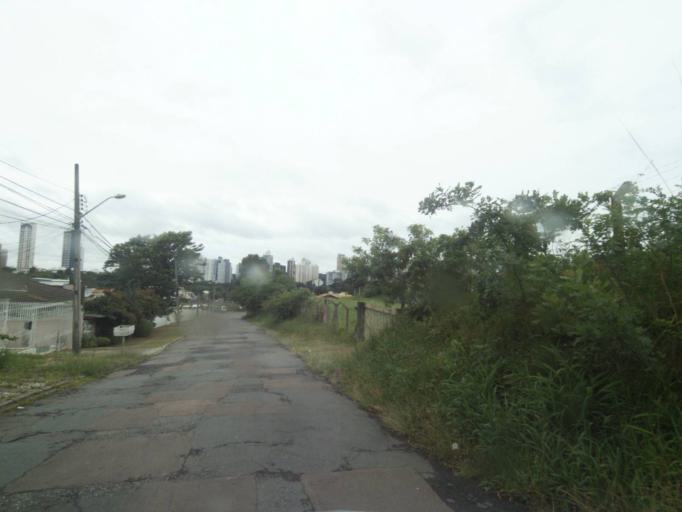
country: BR
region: Parana
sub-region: Curitiba
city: Curitiba
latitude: -25.4291
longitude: -49.3301
